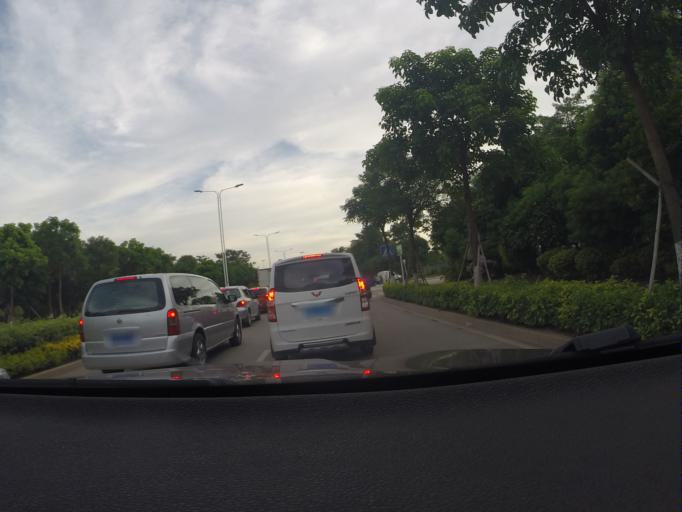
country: CN
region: Guangdong
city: Tangjiawan
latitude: 22.3851
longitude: 113.5447
